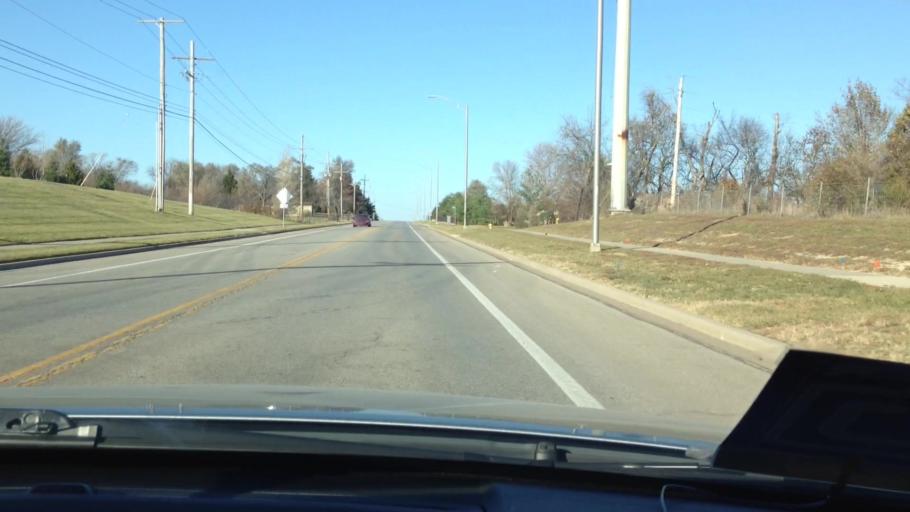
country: US
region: Kansas
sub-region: Johnson County
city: Olathe
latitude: 38.9335
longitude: -94.8161
